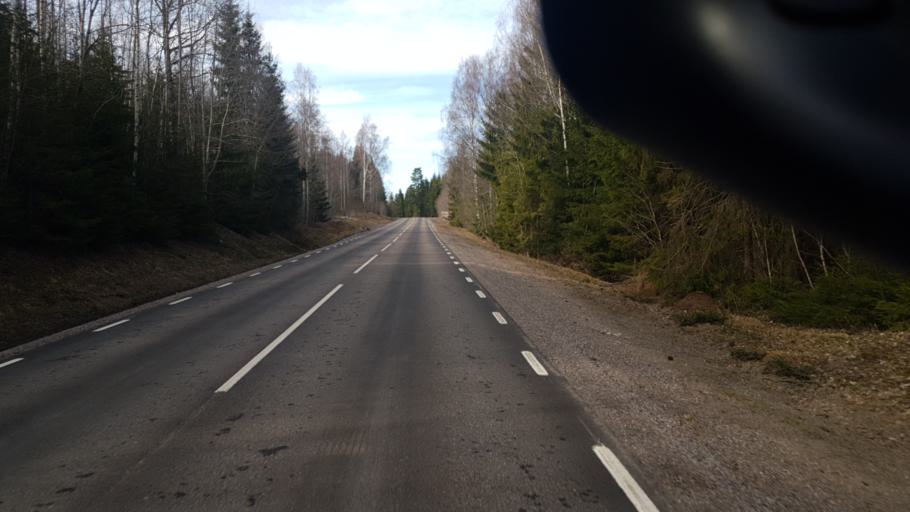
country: SE
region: Vaermland
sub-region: Eda Kommun
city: Amotfors
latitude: 59.7281
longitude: 12.4212
